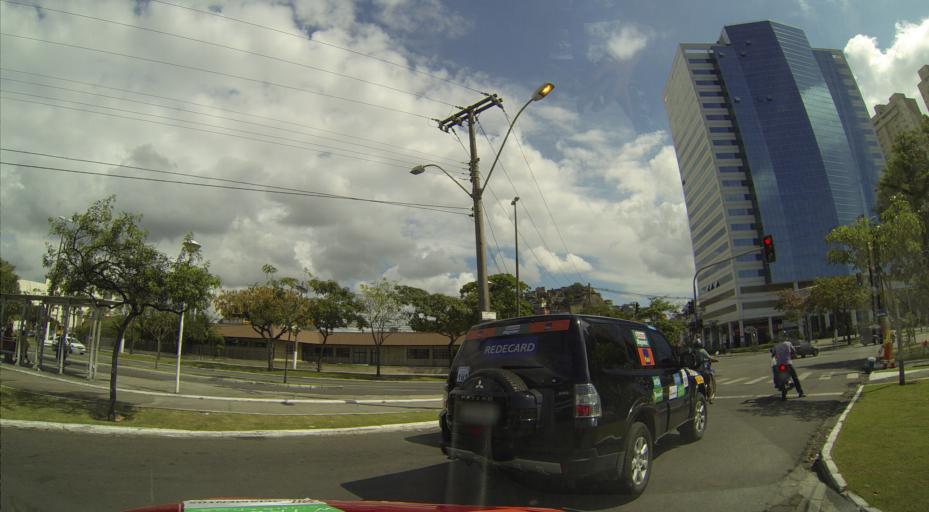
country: BR
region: Espirito Santo
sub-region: Vila Velha
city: Vila Velha
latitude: -20.3166
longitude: -40.2983
